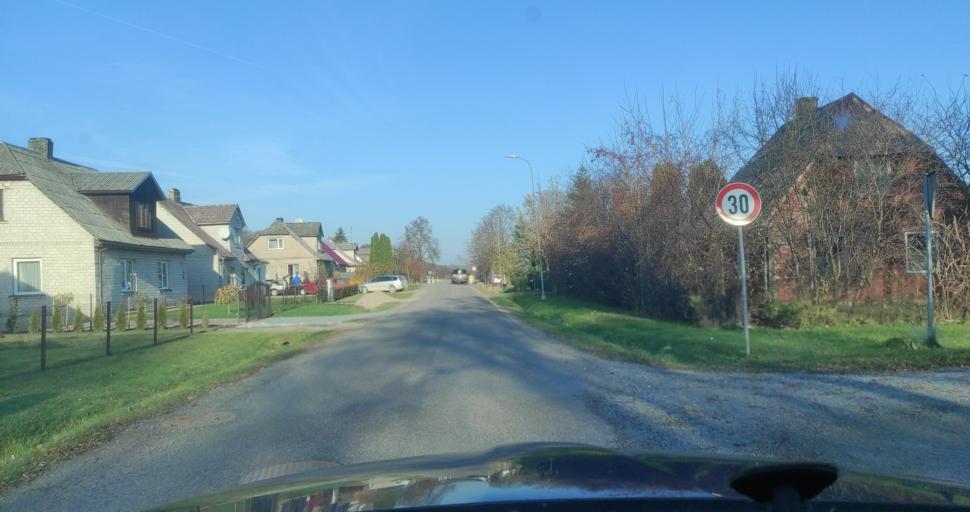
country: LV
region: Saldus Rajons
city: Saldus
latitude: 56.6717
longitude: 22.5027
